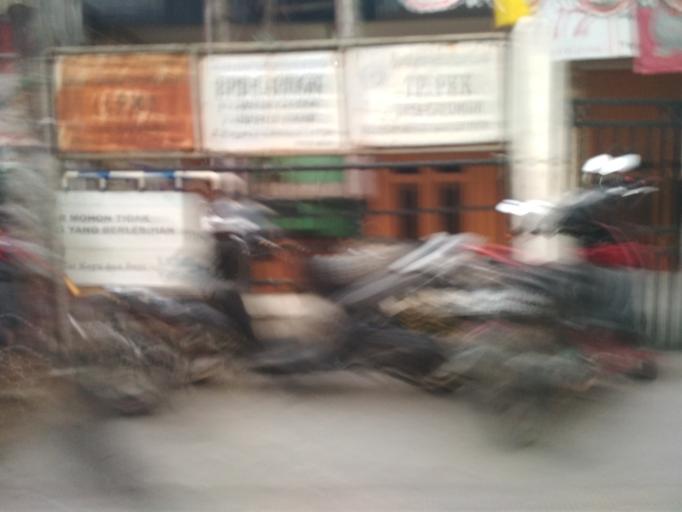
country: ID
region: West Java
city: Caringin
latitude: -6.7063
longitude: 106.8221
